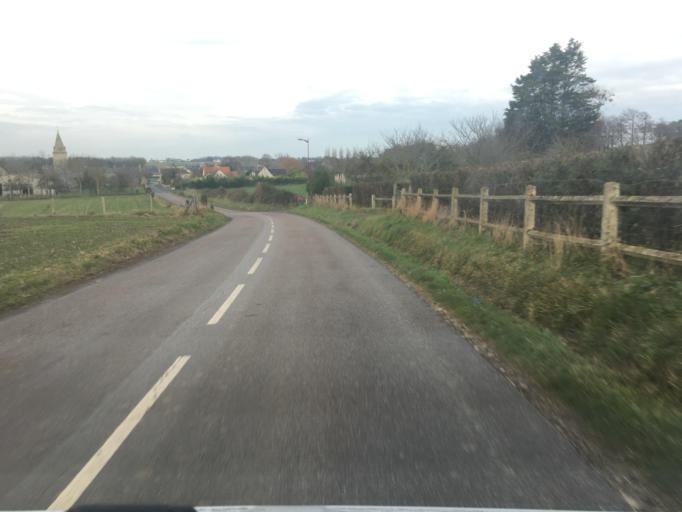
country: FR
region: Lower Normandy
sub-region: Departement du Calvados
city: Ver-sur-Mer
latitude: 49.3251
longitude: -0.5602
